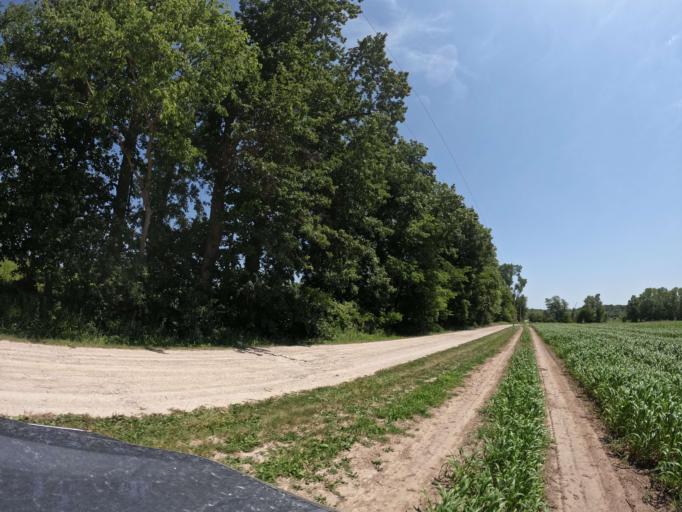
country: US
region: Iowa
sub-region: Henry County
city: Mount Pleasant
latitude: 40.9011
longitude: -91.5624
